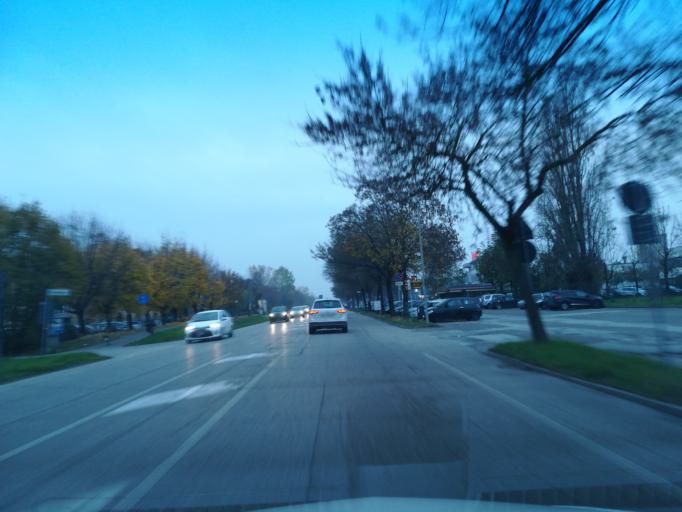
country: IT
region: Emilia-Romagna
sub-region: Provincia di Ravenna
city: Faenza
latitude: 44.3101
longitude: 11.8975
